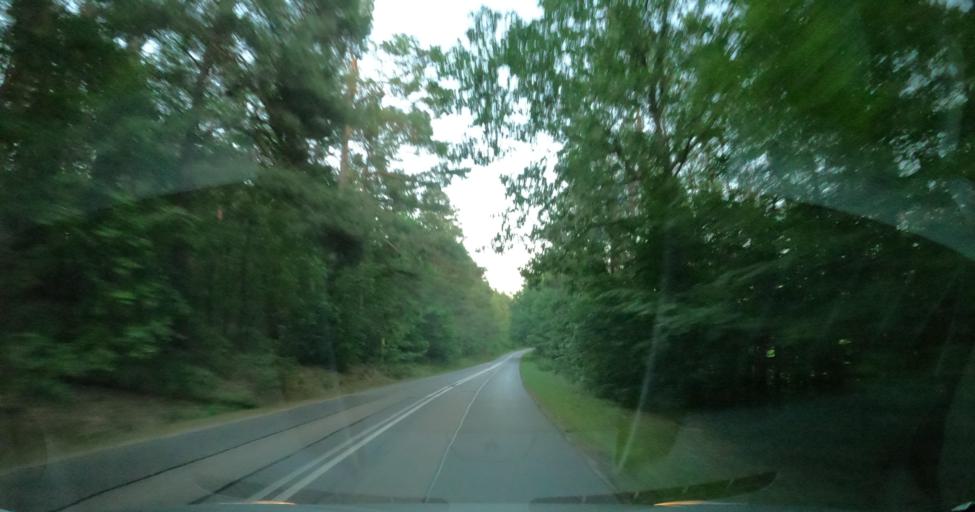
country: PL
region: Pomeranian Voivodeship
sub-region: Powiat wejherowski
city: Linia
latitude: 54.4605
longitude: 18.0005
